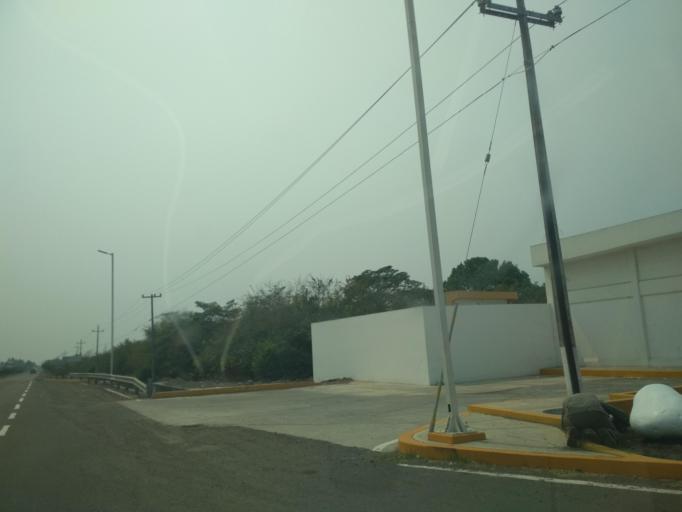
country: MX
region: Veracruz
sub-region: Veracruz
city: Delfino Victoria (Santa Fe)
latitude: 19.1898
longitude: -96.2771
